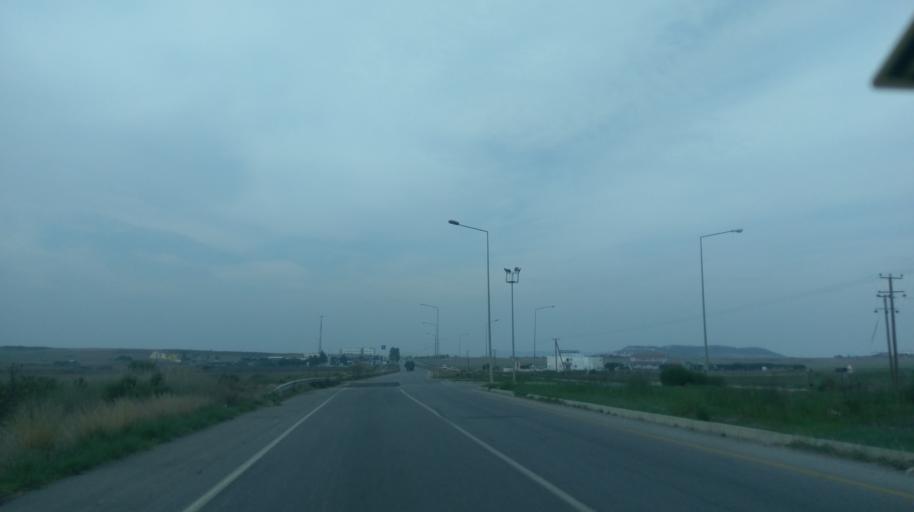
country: CY
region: Lefkosia
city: Mammari
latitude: 35.2120
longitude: 33.2504
